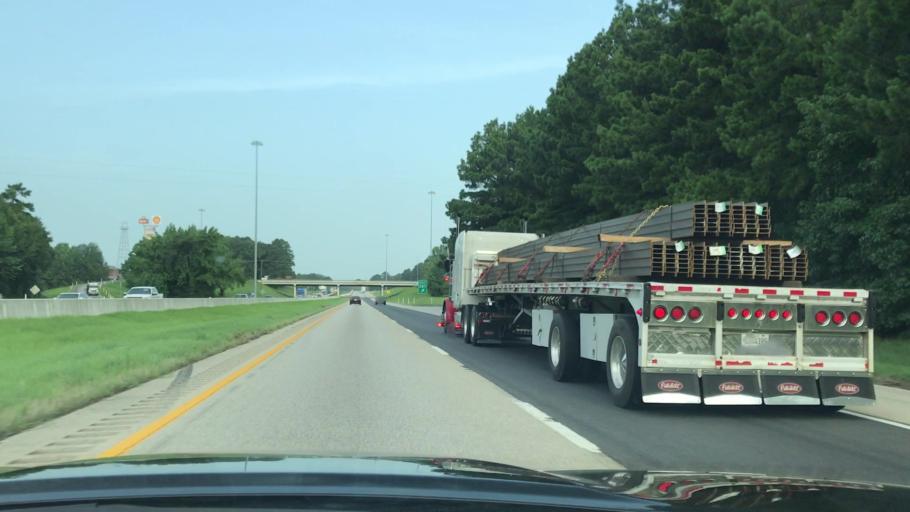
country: US
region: Texas
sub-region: Gregg County
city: Kilgore
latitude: 32.4331
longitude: -94.8581
